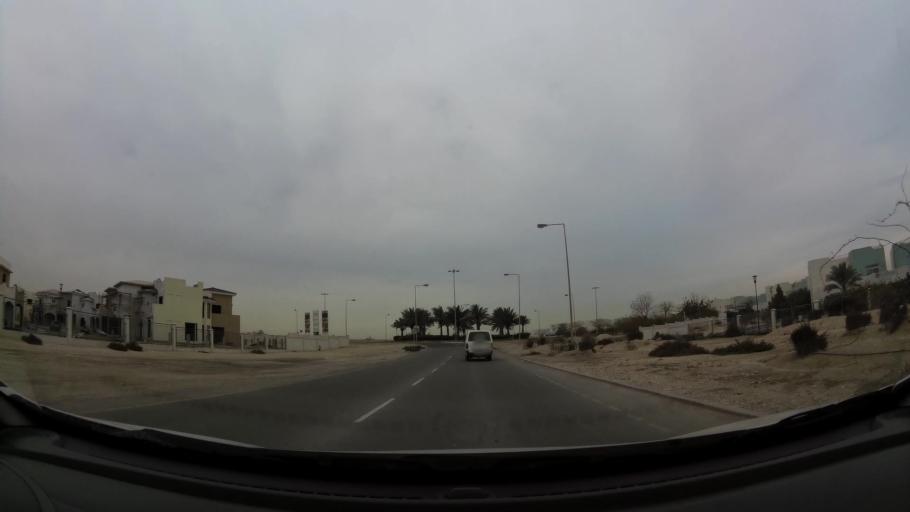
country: BH
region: Northern
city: Ar Rifa'
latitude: 26.0945
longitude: 50.5591
